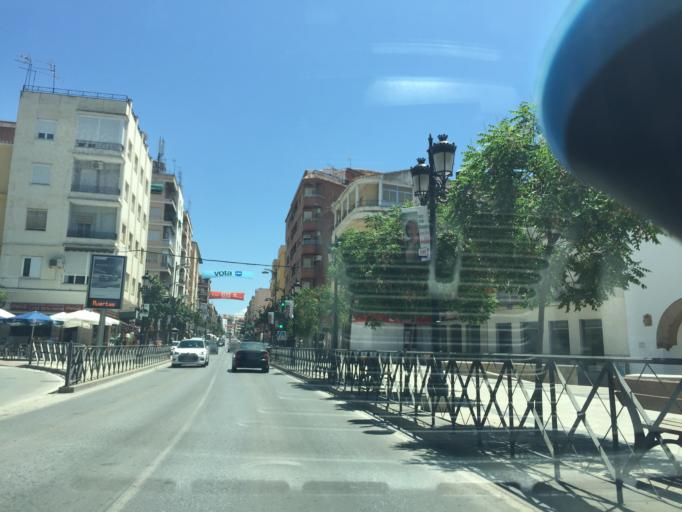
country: ES
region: Andalusia
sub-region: Provincia de Granada
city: Guadix
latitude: 37.3019
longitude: -3.1339
